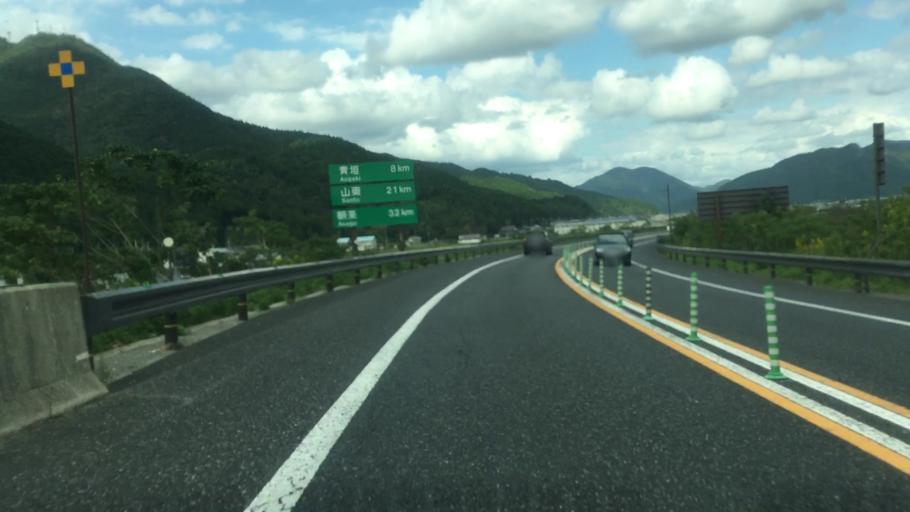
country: JP
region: Kyoto
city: Fukuchiyama
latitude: 35.1801
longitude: 135.0365
